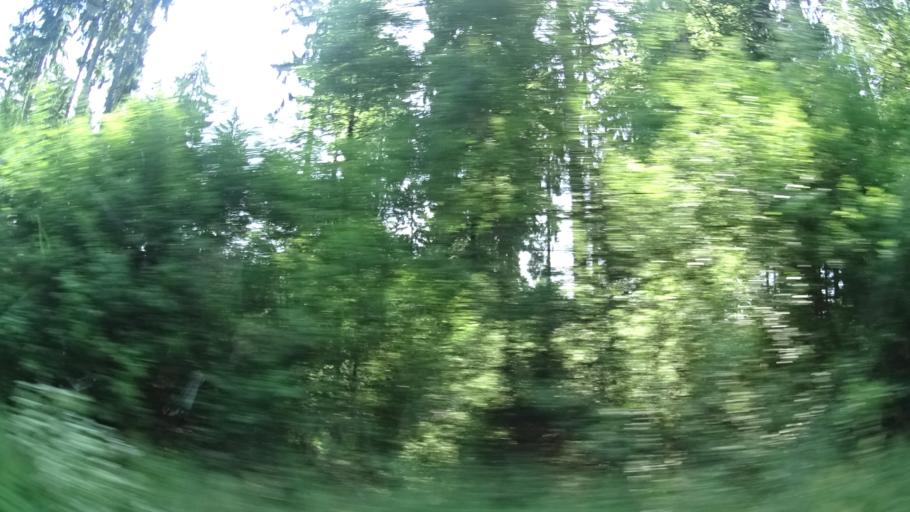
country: DE
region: Hesse
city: Rosenthal
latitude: 50.9376
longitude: 8.8441
